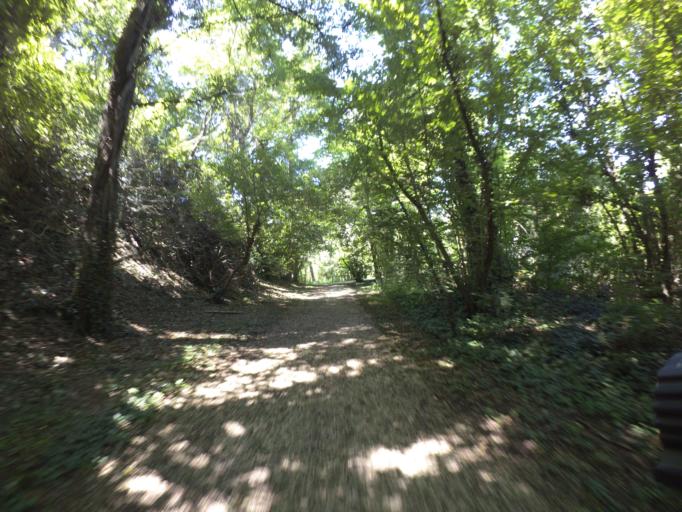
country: IT
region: Friuli Venezia Giulia
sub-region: Provincia di Udine
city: Teor
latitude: 45.8745
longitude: 13.0801
